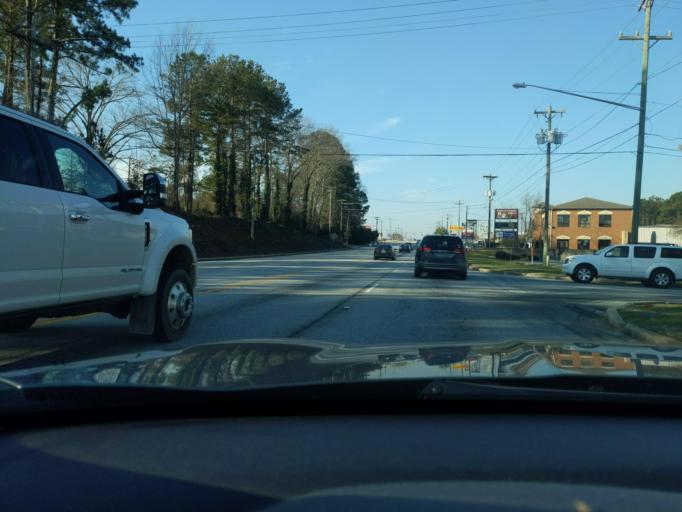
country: US
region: South Carolina
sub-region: Greenwood County
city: Greenwood
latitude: 34.2090
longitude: -82.1839
